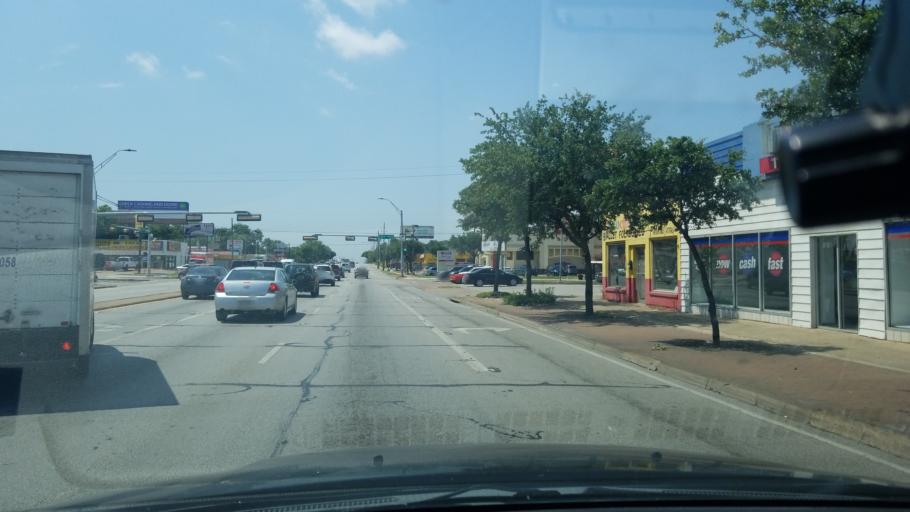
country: US
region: Texas
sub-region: Dallas County
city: Balch Springs
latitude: 32.7350
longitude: -96.6830
